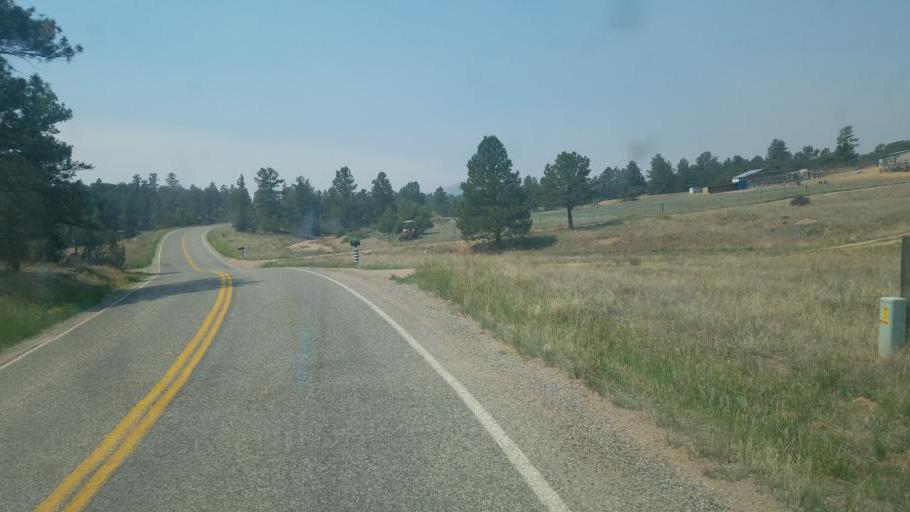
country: US
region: Colorado
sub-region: Fremont County
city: Canon City
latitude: 38.3673
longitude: -105.4618
